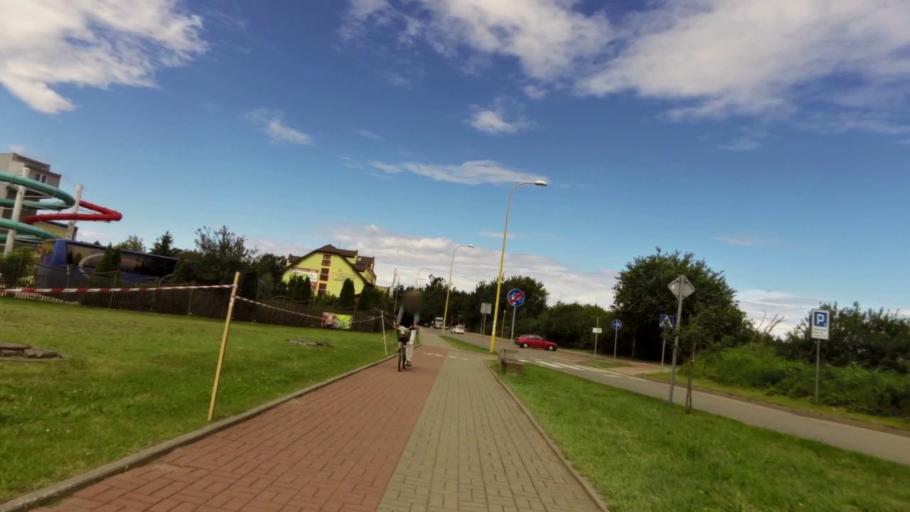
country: PL
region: West Pomeranian Voivodeship
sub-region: Powiat slawienski
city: Darlowo
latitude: 54.4441
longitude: 16.3974
